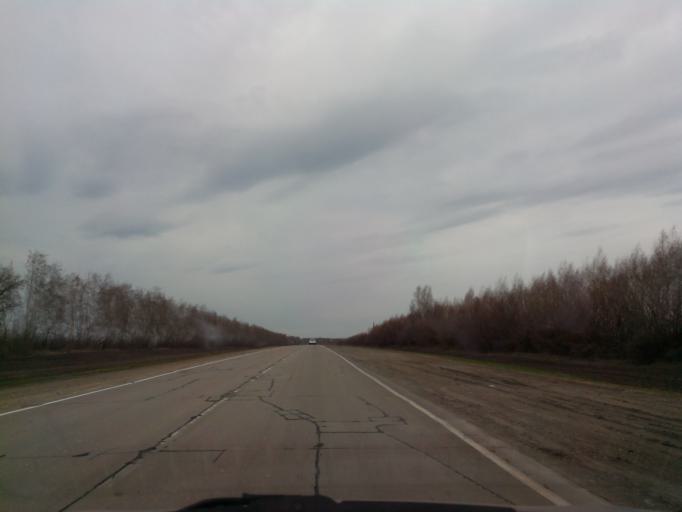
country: RU
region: Tambov
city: Znamenka
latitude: 52.4046
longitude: 41.3882
